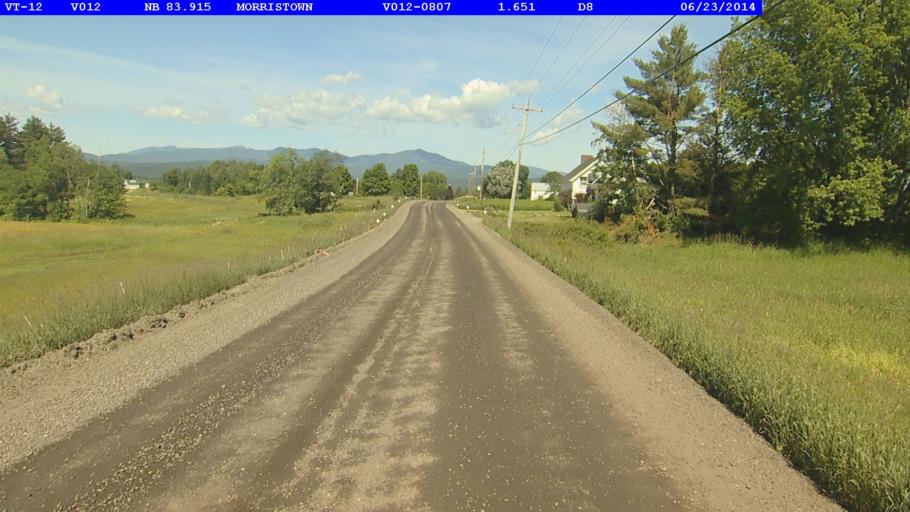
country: US
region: Vermont
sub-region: Lamoille County
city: Morrisville
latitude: 44.5497
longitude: -72.5695
